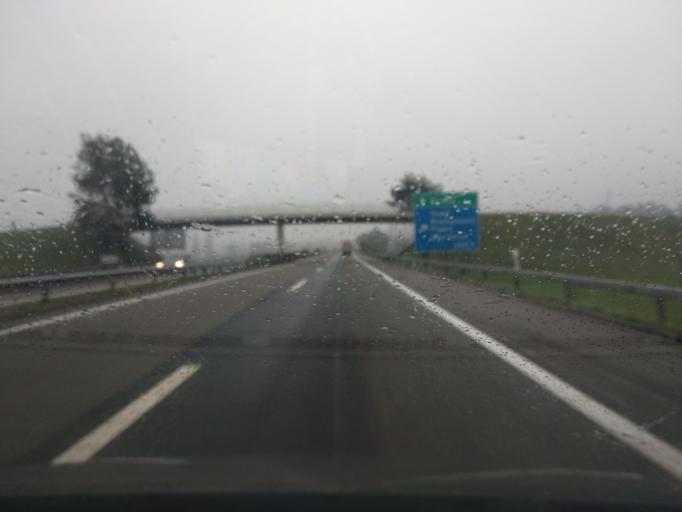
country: CH
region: Saint Gallen
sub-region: Wahlkreis Wil
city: Uzwil
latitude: 47.4529
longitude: 9.1415
